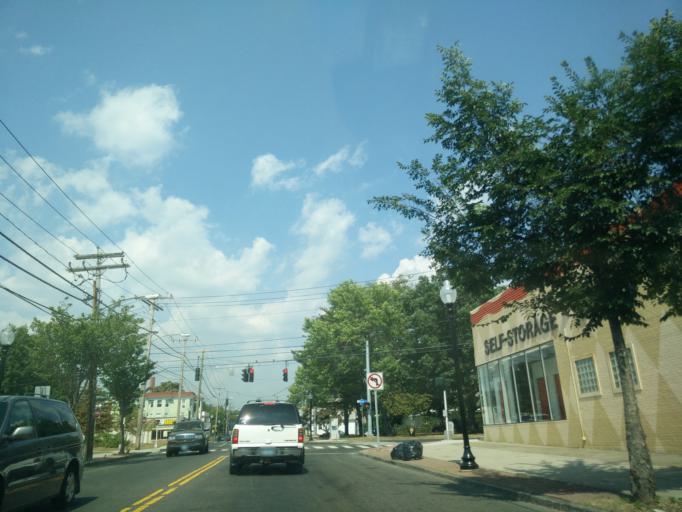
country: US
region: Connecticut
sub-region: Fairfield County
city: Bridgeport
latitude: 41.1975
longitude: -73.1803
